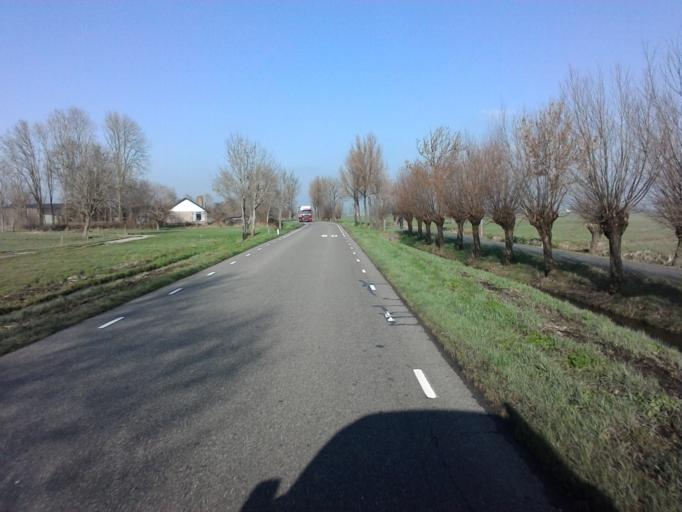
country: NL
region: South Holland
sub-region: Gemeente Gorinchem
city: Gorinchem
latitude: 51.8916
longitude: 4.9831
